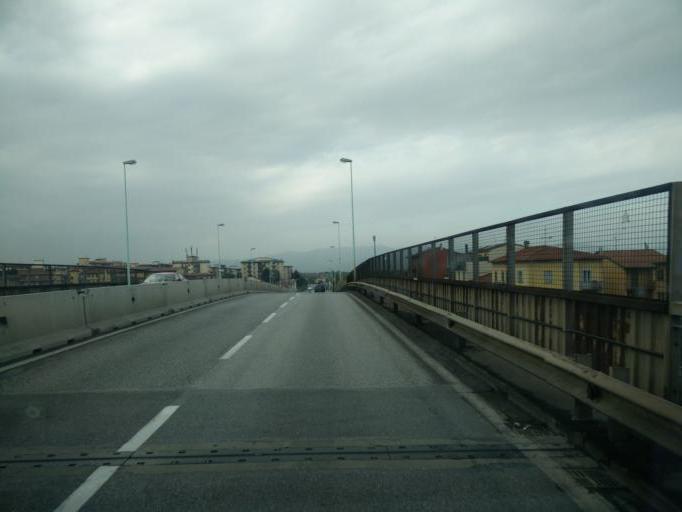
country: IT
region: Tuscany
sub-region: Provincia di Prato
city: Prato
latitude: 43.8921
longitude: 11.0732
